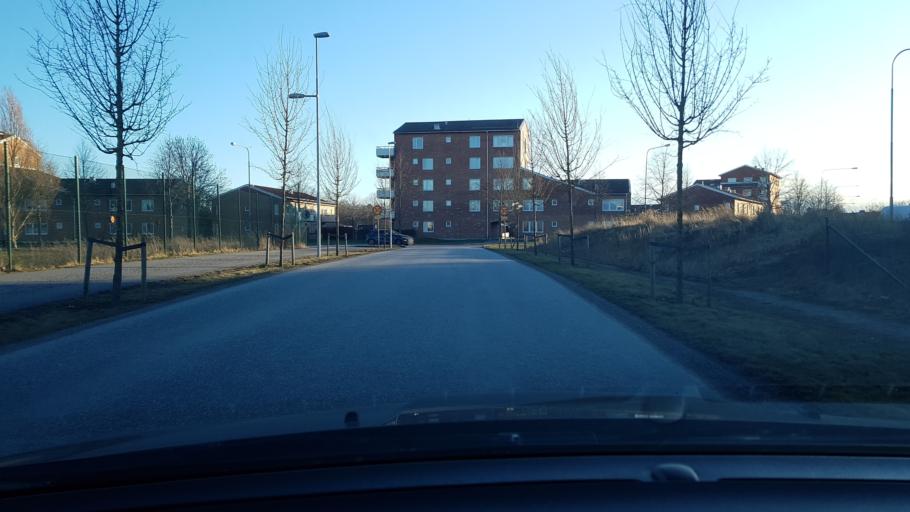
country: SE
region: Stockholm
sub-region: Norrtalje Kommun
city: Norrtalje
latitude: 59.7496
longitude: 18.6943
